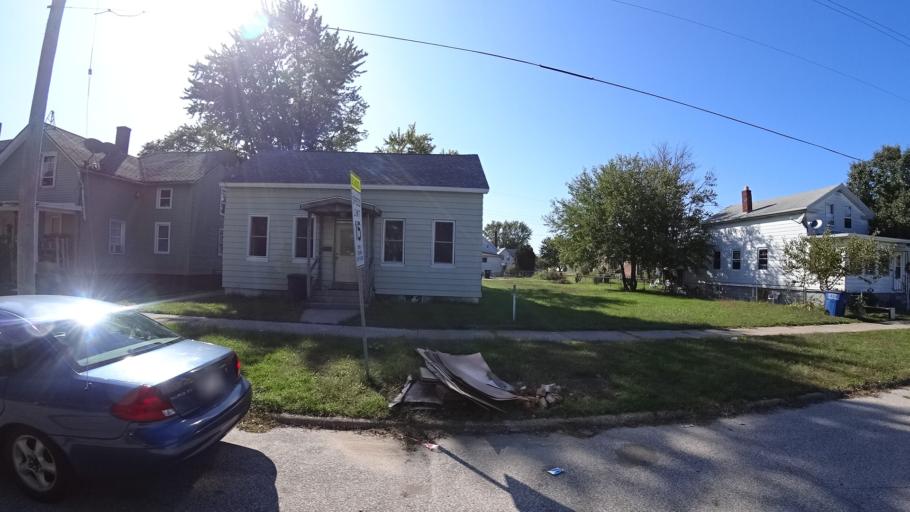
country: US
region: Indiana
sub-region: LaPorte County
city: Michigan City
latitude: 41.7121
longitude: -86.9041
